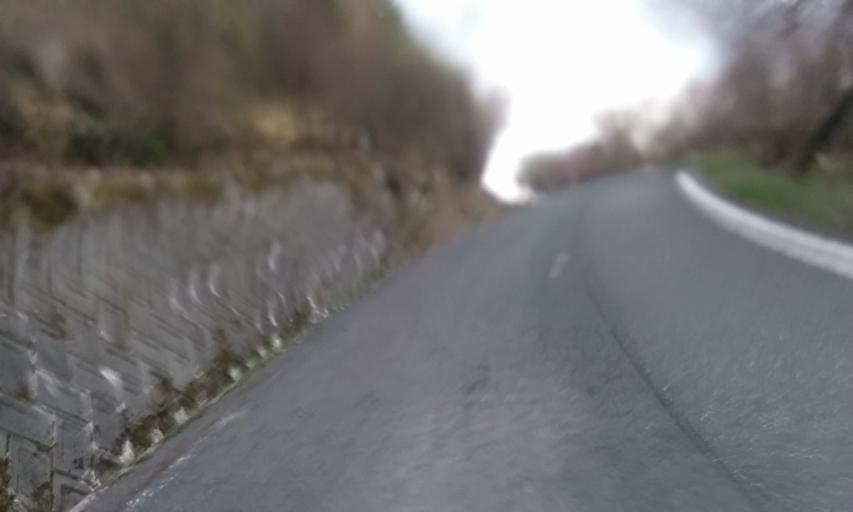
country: JP
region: Ehime
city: Saijo
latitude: 33.7798
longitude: 133.2187
